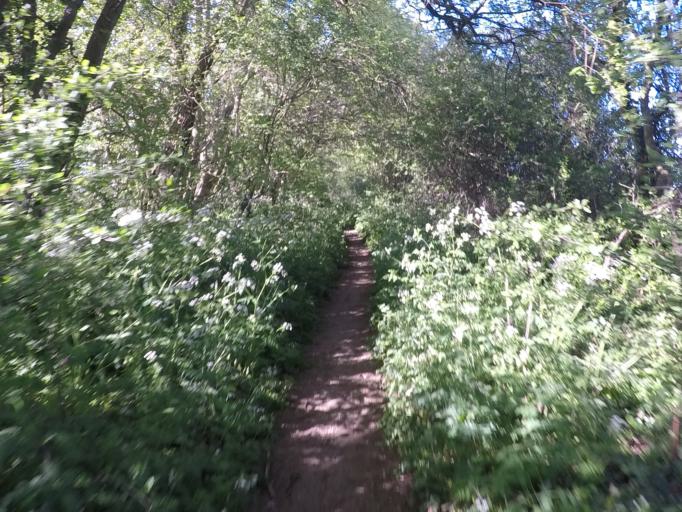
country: GB
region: England
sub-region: Oxfordshire
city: Stonesfield
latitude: 51.8585
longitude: -1.4383
